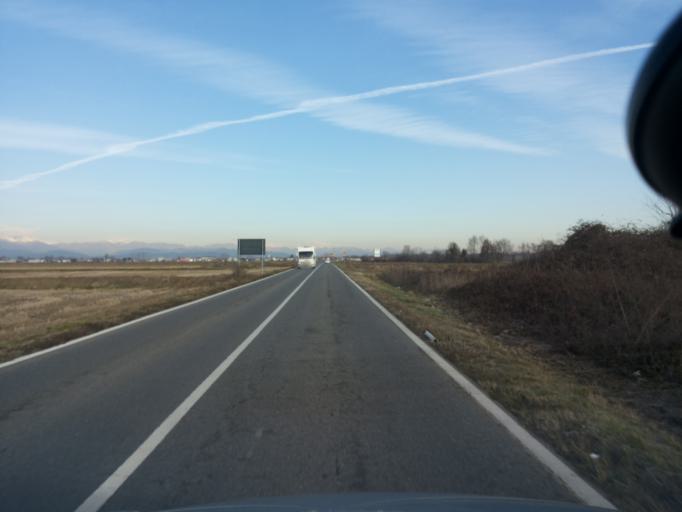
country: IT
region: Piedmont
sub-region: Provincia di Vercelli
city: Arborio
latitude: 45.4773
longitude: 8.3876
